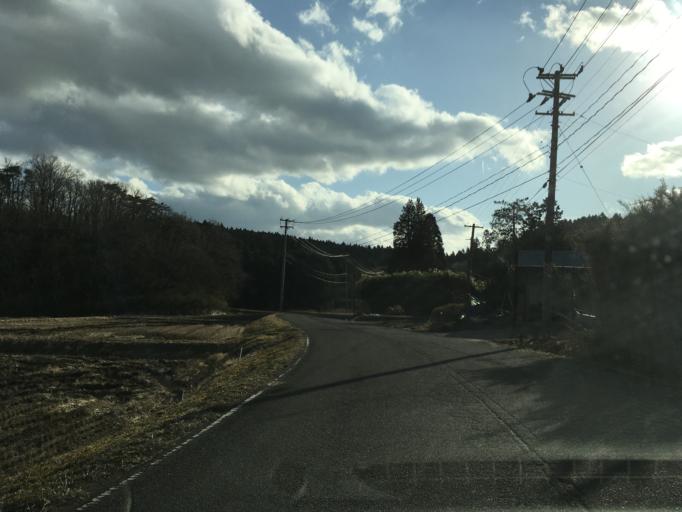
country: JP
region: Iwate
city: Ichinoseki
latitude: 38.8155
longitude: 140.9981
